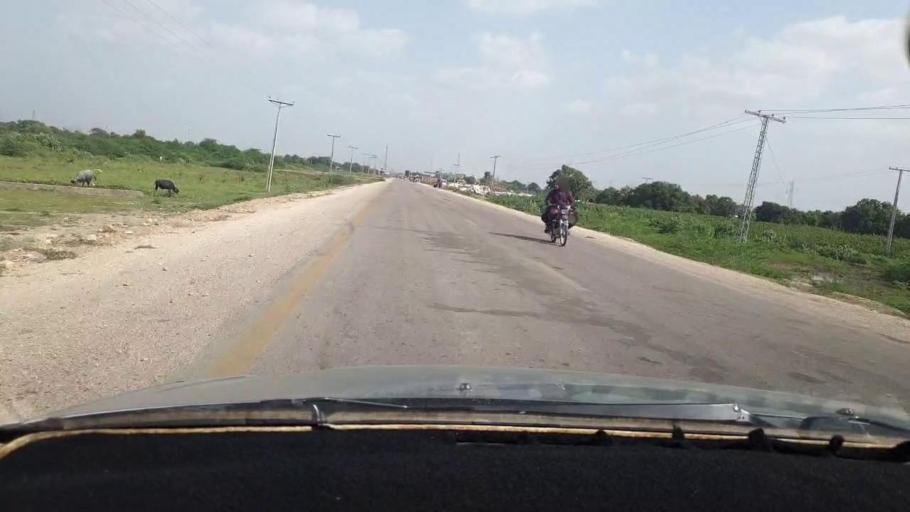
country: PK
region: Sindh
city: Naukot
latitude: 24.8626
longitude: 69.3892
